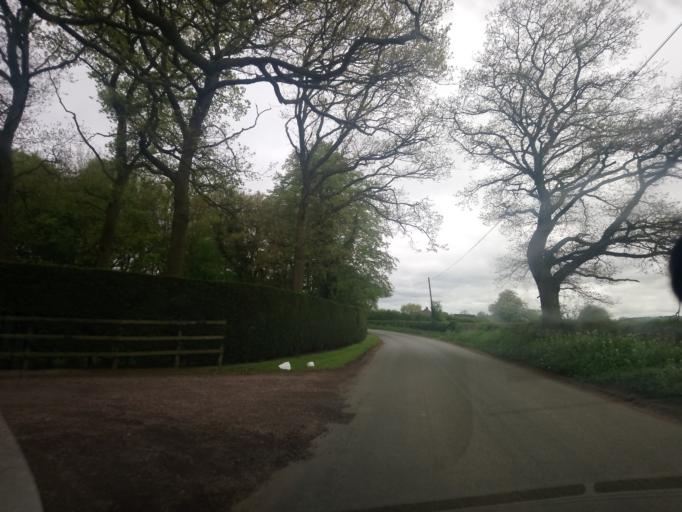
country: GB
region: England
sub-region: Shropshire
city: Stoke upon Tern
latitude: 52.8506
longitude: -2.5251
